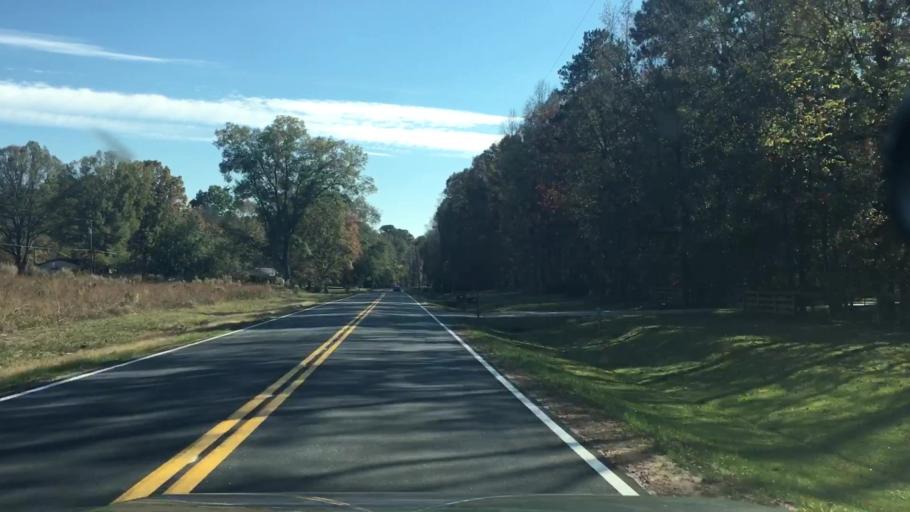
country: US
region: Georgia
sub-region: Coweta County
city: East Newnan
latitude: 33.3488
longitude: -84.7145
